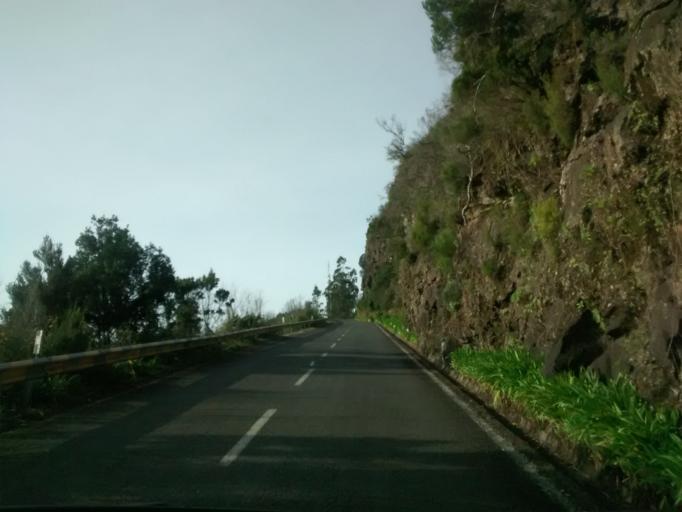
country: PT
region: Madeira
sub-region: Sao Vicente
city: Sao Vicente
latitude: 32.7523
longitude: -17.0297
